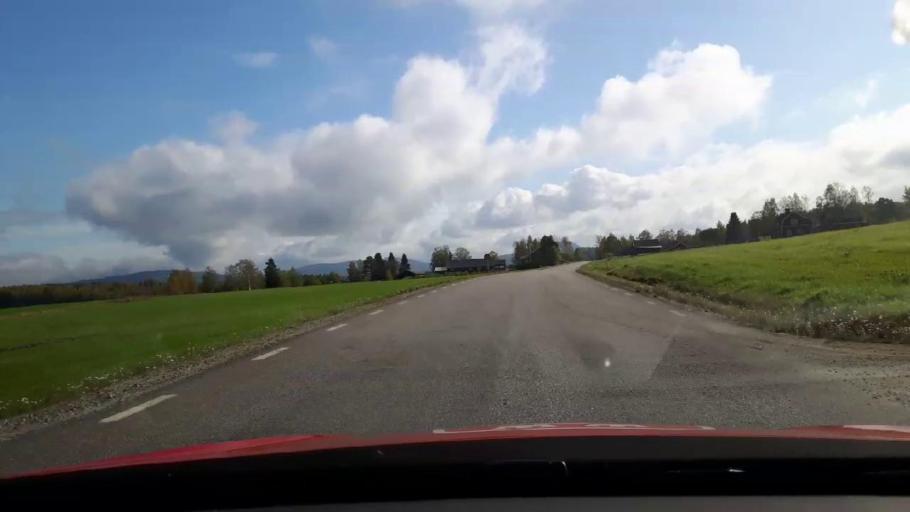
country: SE
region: Gaevleborg
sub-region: Ljusdals Kommun
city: Jaervsoe
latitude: 61.7563
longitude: 16.1170
